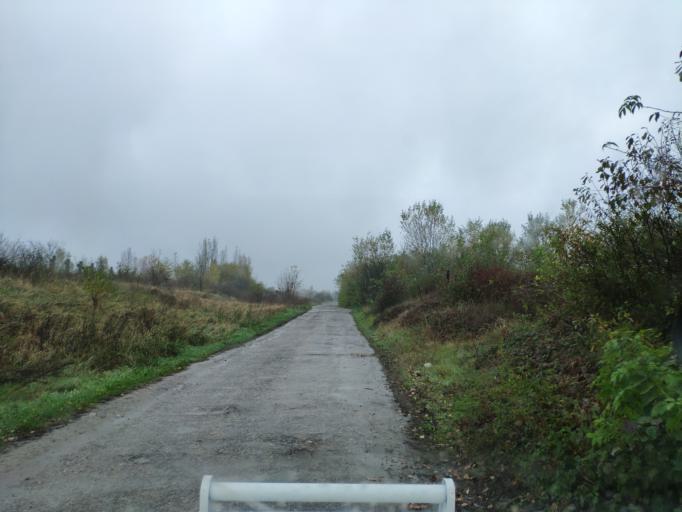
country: SK
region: Kosicky
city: Cierna nad Tisou
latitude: 48.4212
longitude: 21.9942
